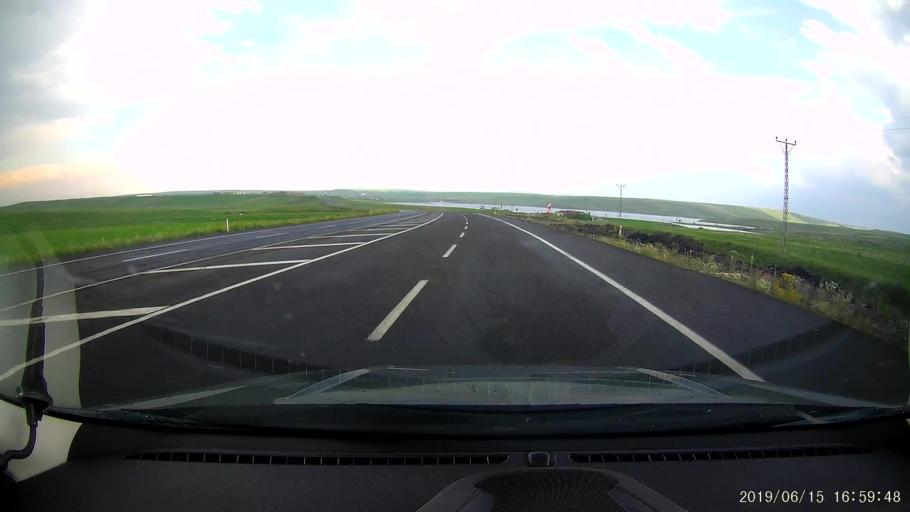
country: TR
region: Kars
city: Susuz
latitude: 40.7468
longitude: 43.1533
